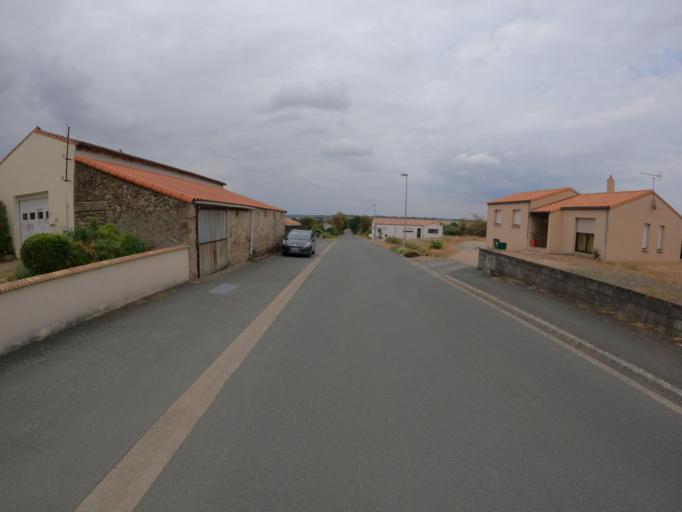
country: FR
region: Pays de la Loire
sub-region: Departement de la Vendee
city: Les Landes-Genusson
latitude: 46.9680
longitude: -1.1160
